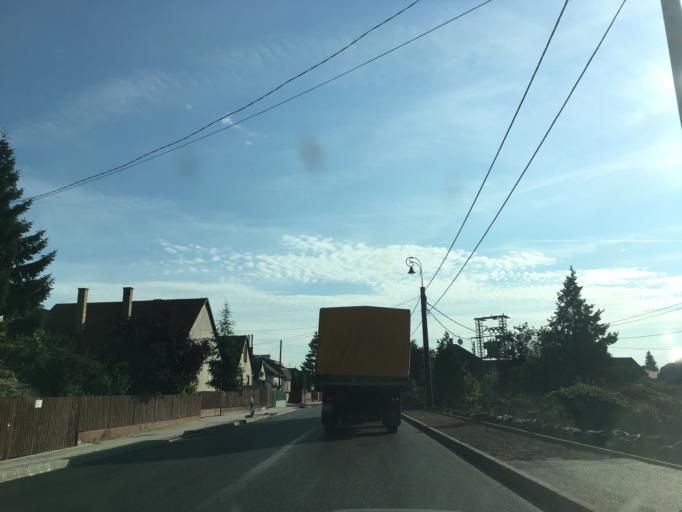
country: HU
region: Hajdu-Bihar
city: Nyiradony
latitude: 47.6875
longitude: 21.8999
